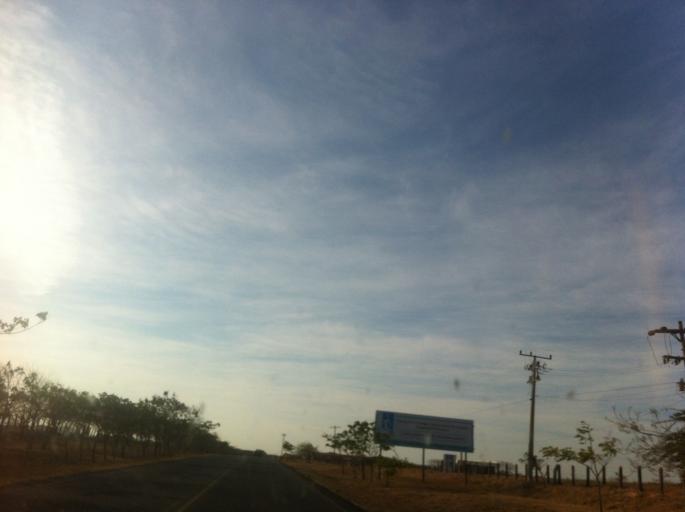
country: NI
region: Rivas
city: Rivas
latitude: 11.3444
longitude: -85.7358
